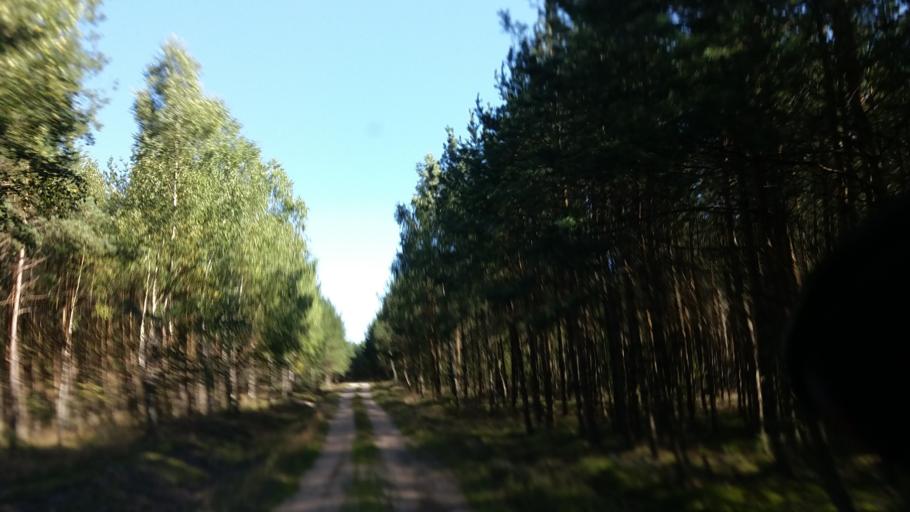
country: PL
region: West Pomeranian Voivodeship
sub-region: Powiat szczecinecki
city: Borne Sulinowo
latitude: 53.5713
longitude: 16.4900
